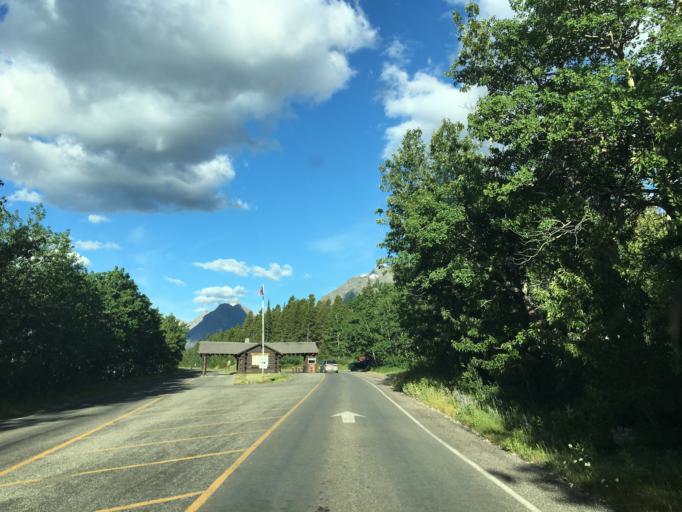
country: CA
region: Alberta
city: Cardston
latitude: 48.8225
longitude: -113.5784
